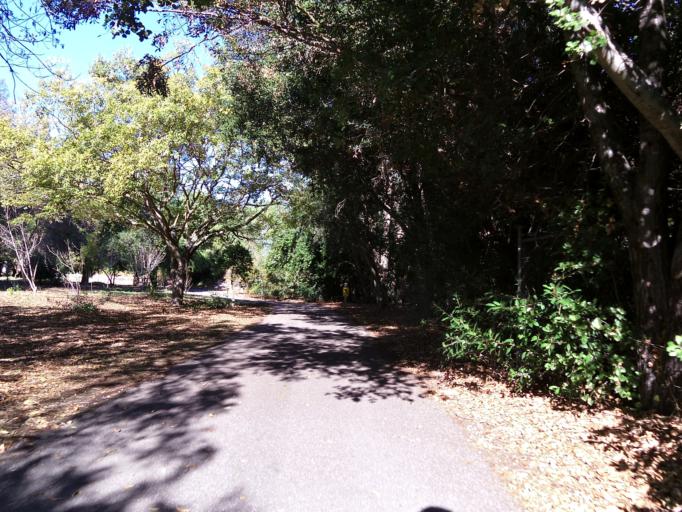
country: US
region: California
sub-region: Santa Clara County
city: Mountain View
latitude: 37.3876
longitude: -122.0695
